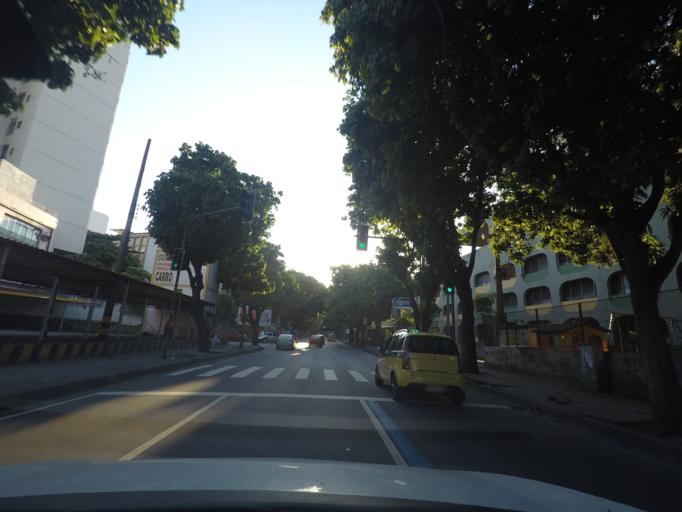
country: BR
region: Rio de Janeiro
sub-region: Rio De Janeiro
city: Rio de Janeiro
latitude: -22.9214
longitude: -43.2277
